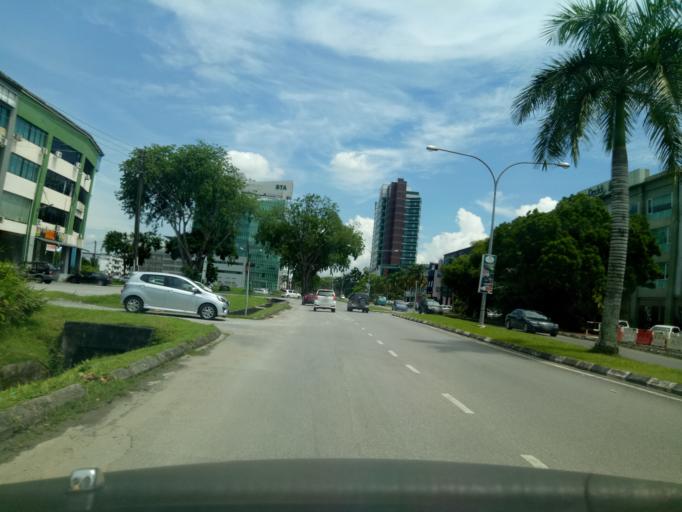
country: MY
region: Sarawak
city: Kuching
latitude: 1.5524
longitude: 110.3708
